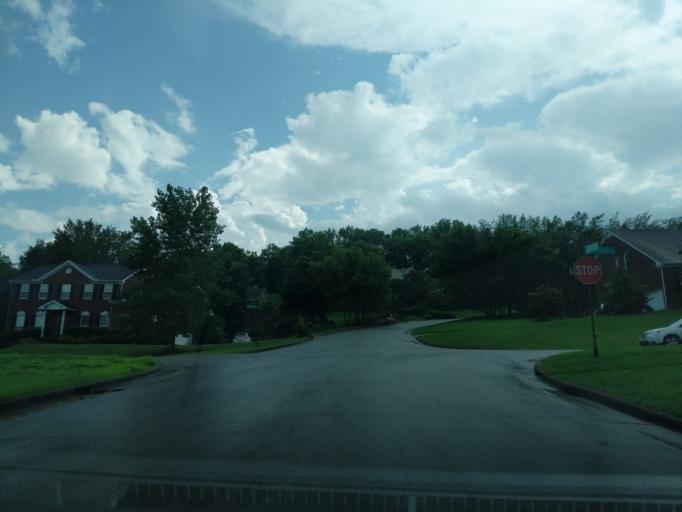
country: US
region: Tennessee
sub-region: Davidson County
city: Belle Meade
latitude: 36.0440
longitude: -86.9436
